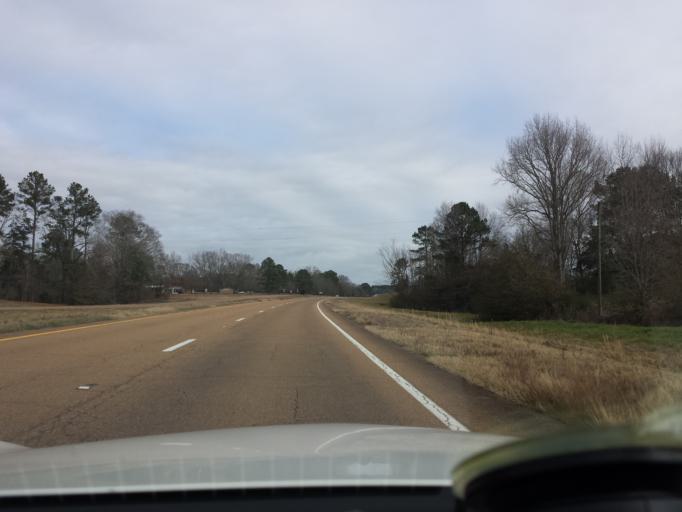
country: US
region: Mississippi
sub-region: Leake County
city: Carthage
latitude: 32.8521
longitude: -89.4582
